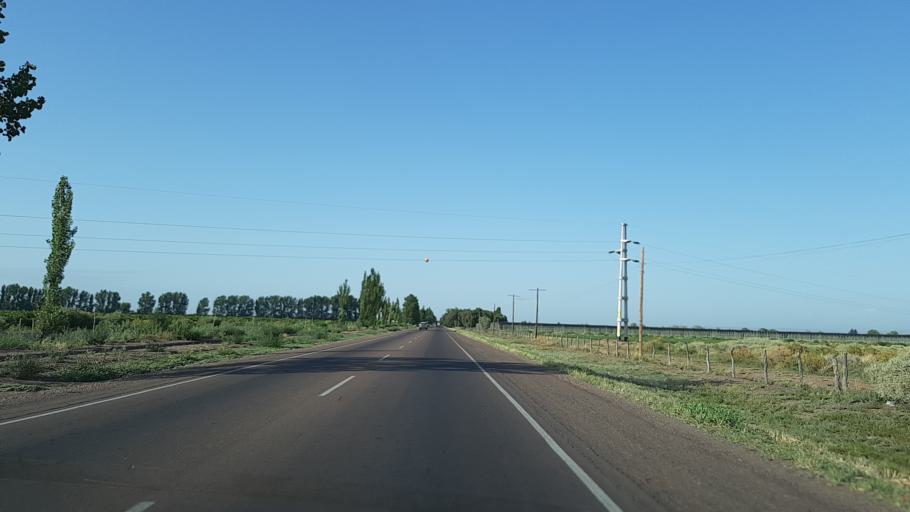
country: AR
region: Mendoza
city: San Martin
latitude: -33.0011
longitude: -68.4802
